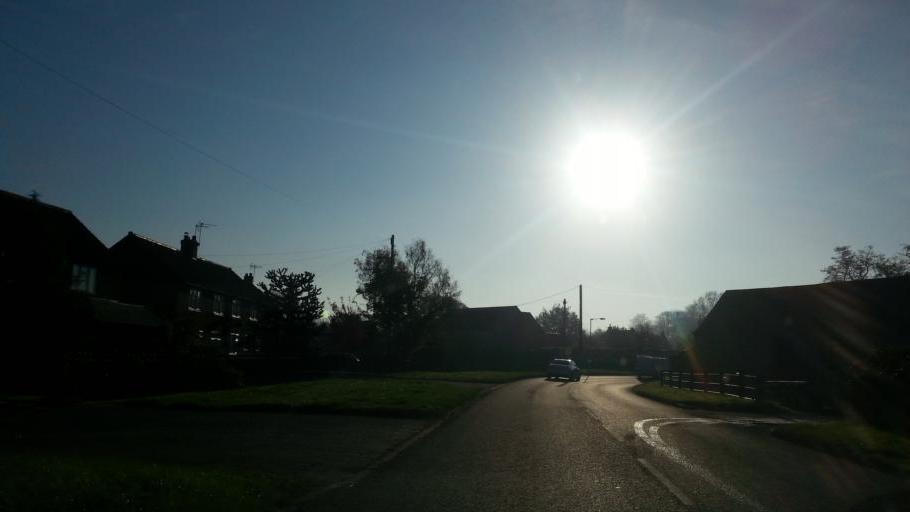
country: GB
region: England
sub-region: Nottinghamshire
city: Newark on Trent
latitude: 53.0944
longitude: -0.8458
